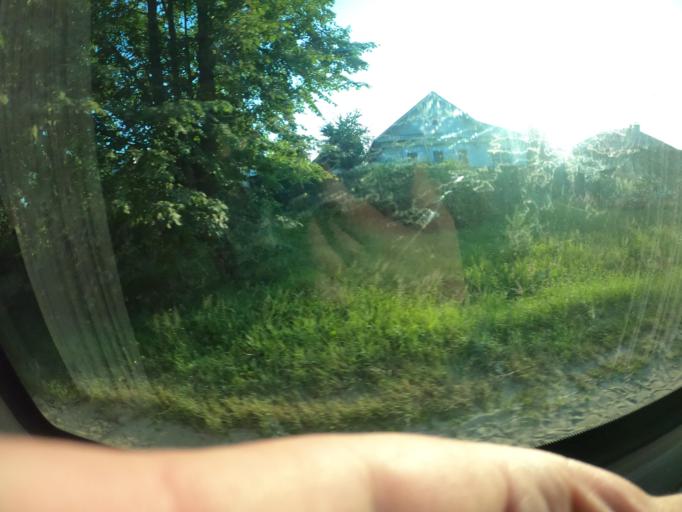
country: RU
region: Moskovskaya
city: Serpukhov
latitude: 54.9307
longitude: 37.3679
